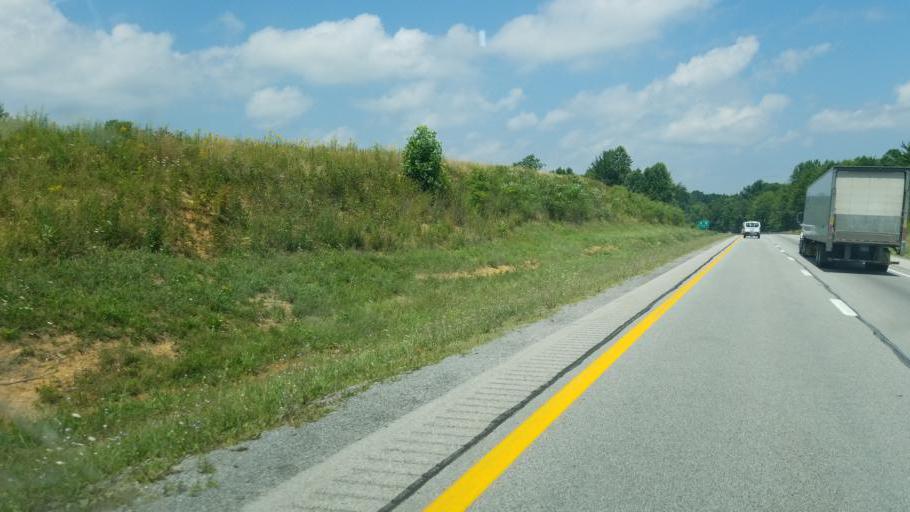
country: US
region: West Virginia
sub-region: Mercer County
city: Athens
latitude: 37.4031
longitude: -81.0612
